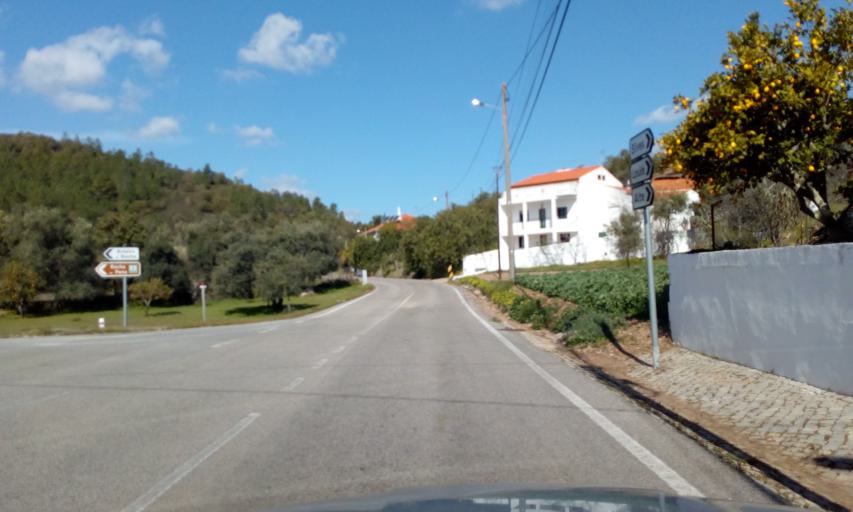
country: PT
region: Faro
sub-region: Loule
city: Loule
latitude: 37.2462
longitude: -8.0683
